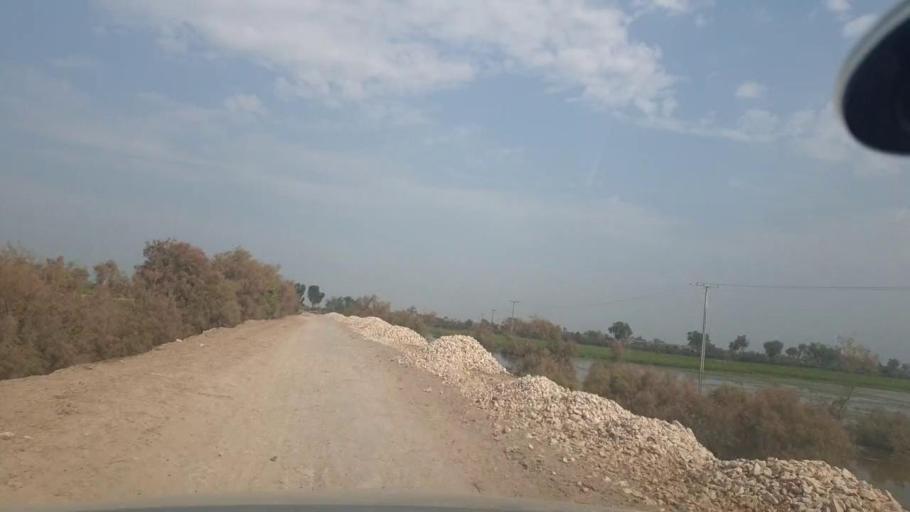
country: PK
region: Balochistan
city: Mehrabpur
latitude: 28.0702
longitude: 68.1020
